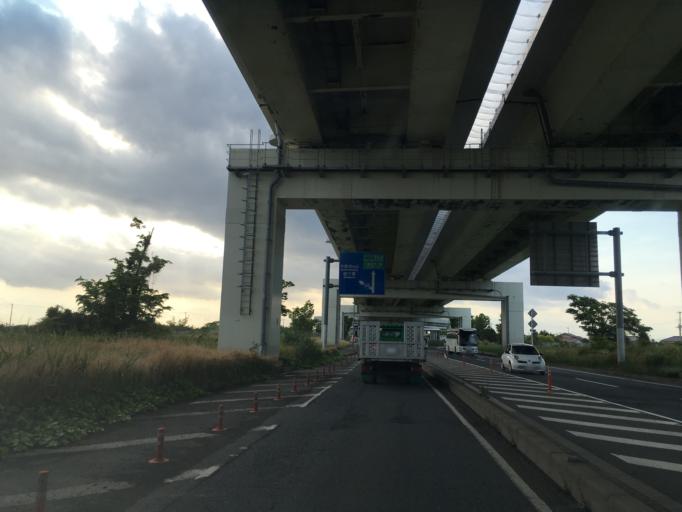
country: JP
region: Chiba
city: Kisarazu
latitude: 35.4132
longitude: 139.9552
